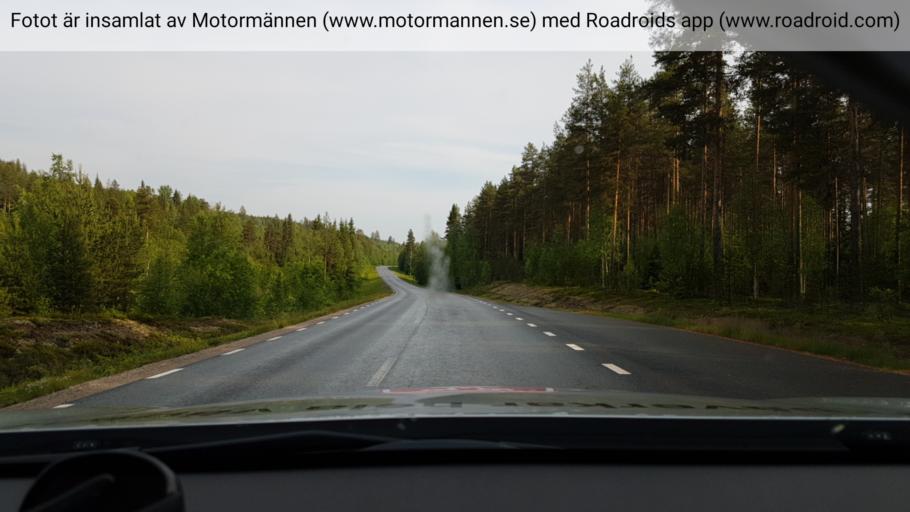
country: SE
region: Vaesterbotten
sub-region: Bjurholms Kommun
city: Bjurholm
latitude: 64.3350
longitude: 19.1480
